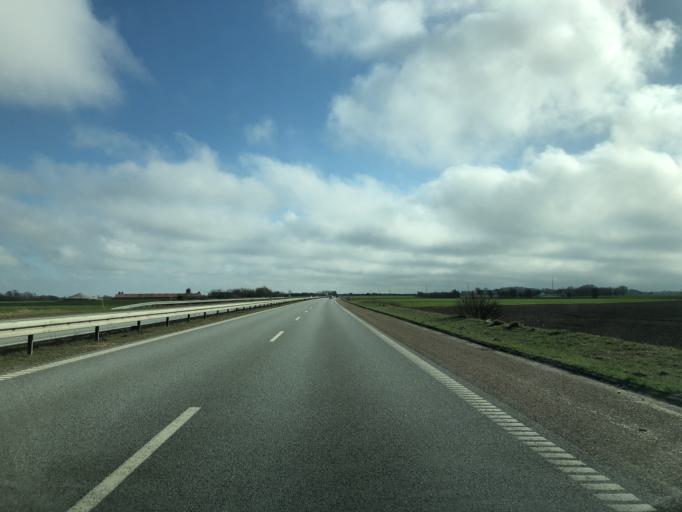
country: DK
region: North Denmark
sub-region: Hjorring Kommune
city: Hjorring
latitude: 57.4444
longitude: 10.0404
